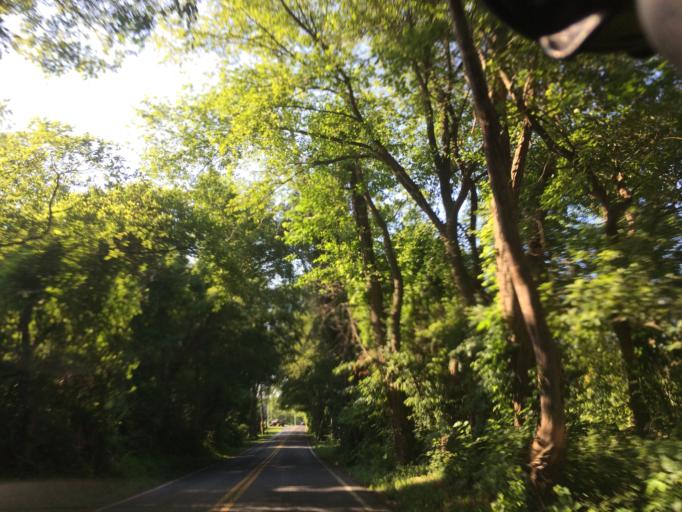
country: US
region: Maryland
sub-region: Montgomery County
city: Olney
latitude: 39.2558
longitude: -77.0629
